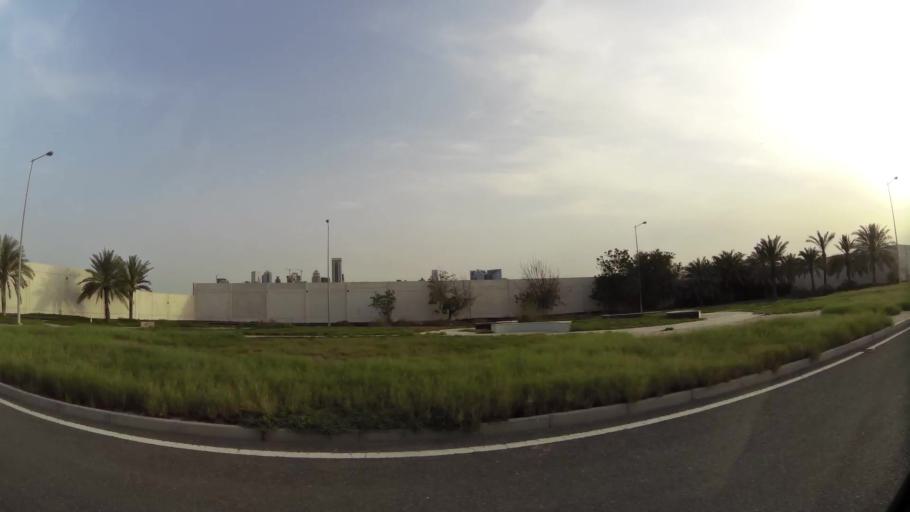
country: QA
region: Baladiyat ad Dawhah
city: Doha
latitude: 25.3463
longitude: 51.5295
